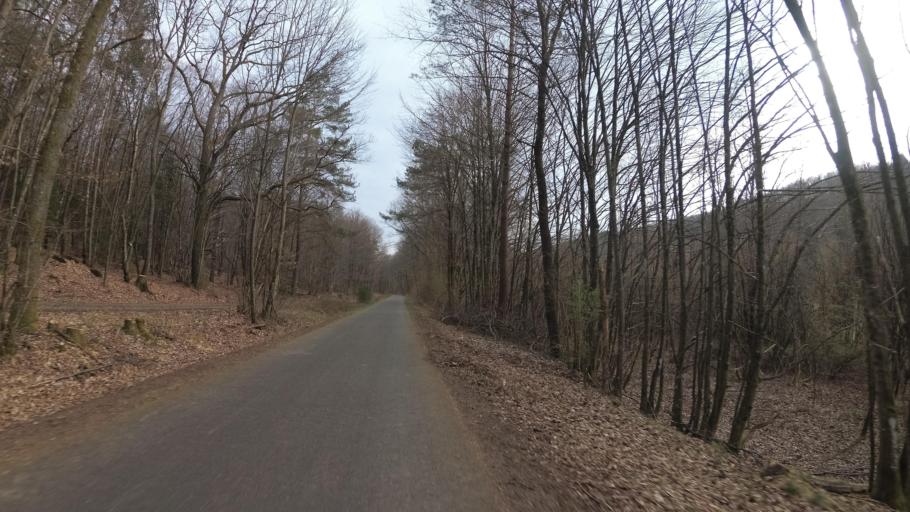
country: DE
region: Rheinland-Pfalz
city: Ellweiler
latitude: 49.6201
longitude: 7.1611
